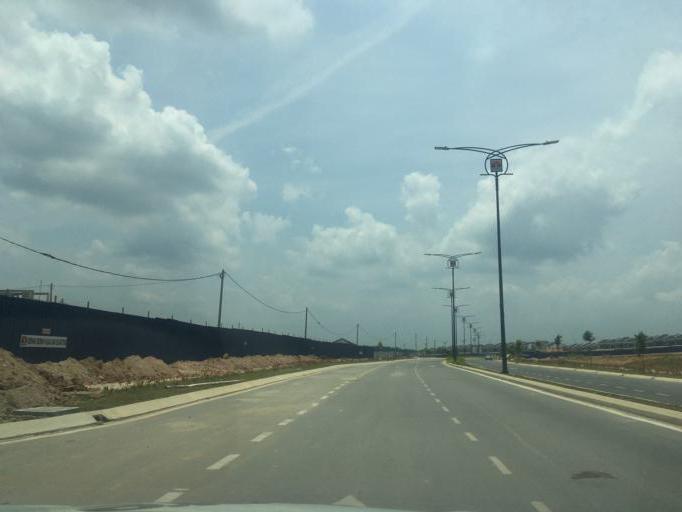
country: MY
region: Putrajaya
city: Putrajaya
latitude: 2.8509
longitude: 101.7051
